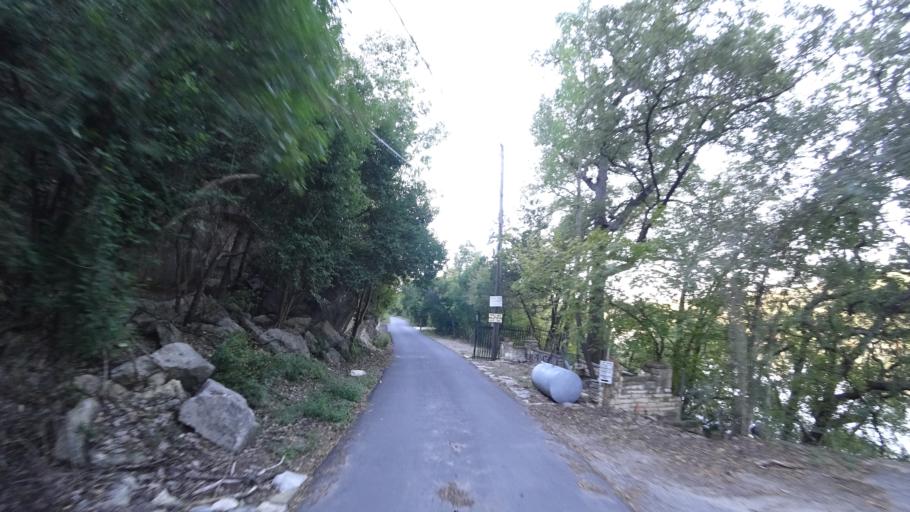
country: US
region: Texas
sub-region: Travis County
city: West Lake Hills
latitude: 30.3467
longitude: -97.8095
